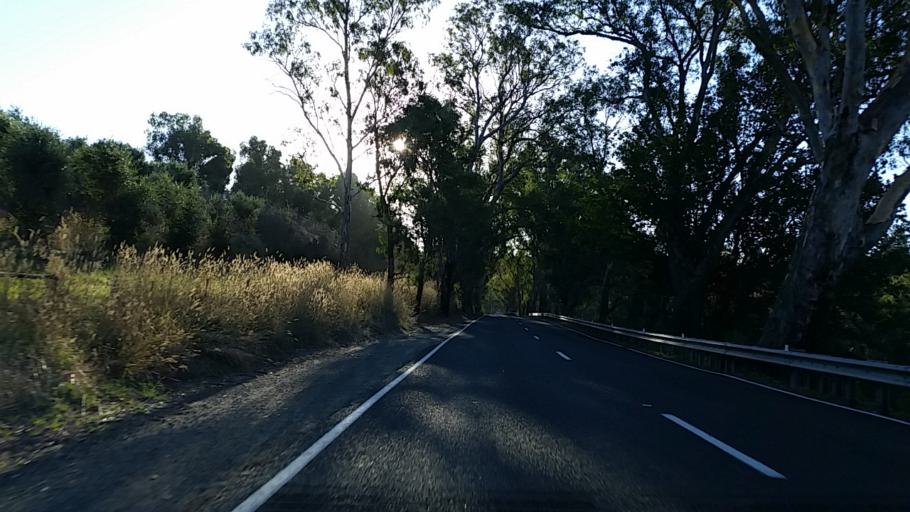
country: AU
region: South Australia
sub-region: Adelaide Hills
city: Gumeracha
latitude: -34.8205
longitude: 138.8648
